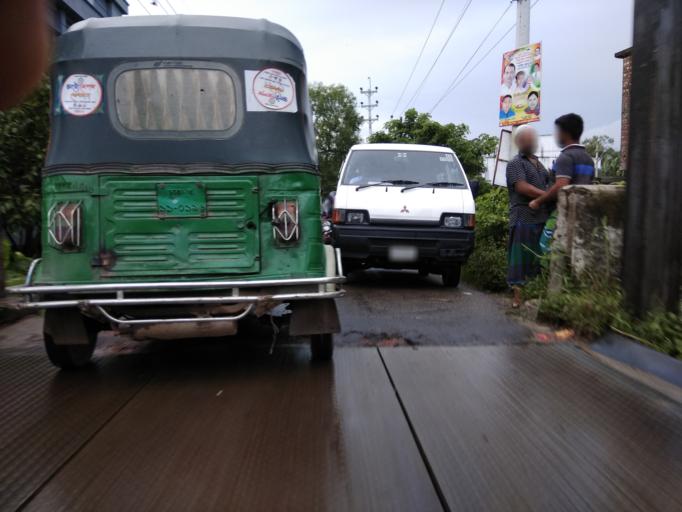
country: BD
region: Dhaka
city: Azimpur
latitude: 23.6981
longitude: 90.3339
